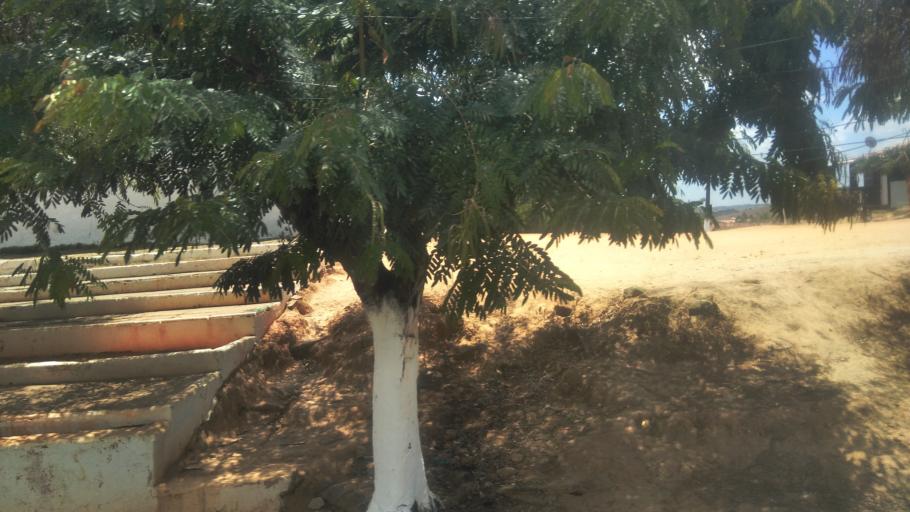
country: BR
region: Pernambuco
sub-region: Vicencia
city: Vicencia
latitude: -7.7260
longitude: -35.3249
